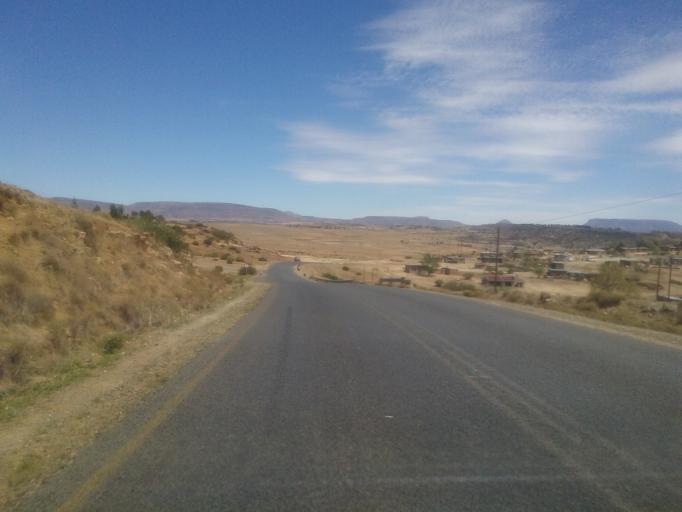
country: LS
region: Mohale's Hoek District
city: Mohale's Hoek
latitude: -30.0640
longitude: 27.4183
